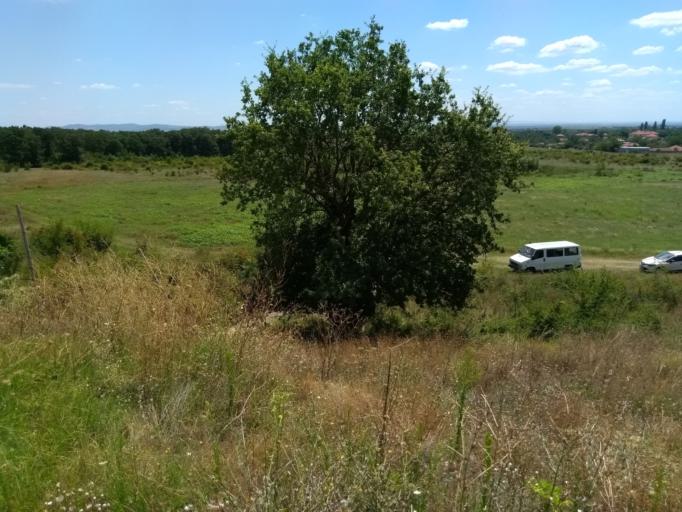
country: BG
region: Sliven
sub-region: Obshtina Nova Zagora
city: Nova Zagora
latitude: 42.5209
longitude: 25.9139
